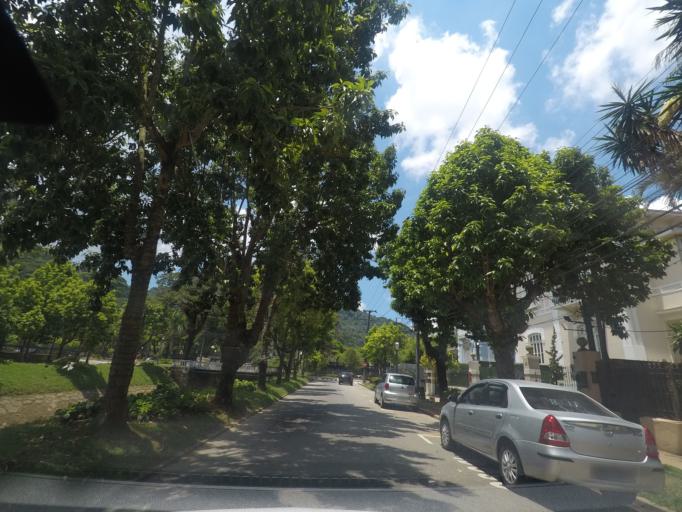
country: BR
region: Rio de Janeiro
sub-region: Petropolis
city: Petropolis
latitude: -22.5068
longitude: -43.1800
